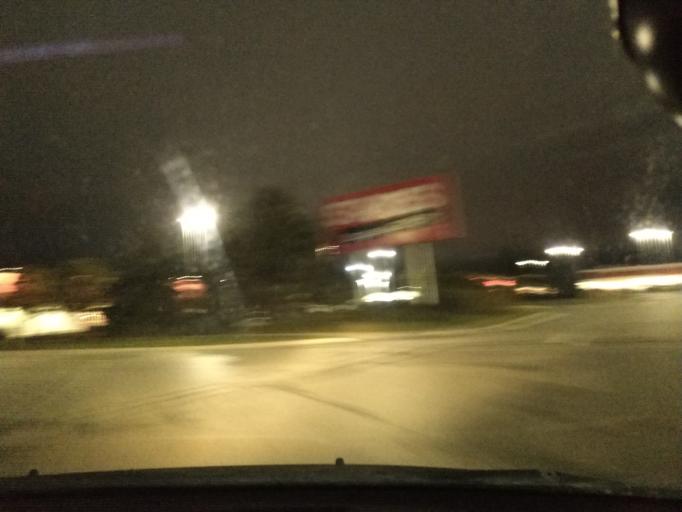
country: CA
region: Ontario
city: Innisfil
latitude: 44.3375
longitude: -79.6878
